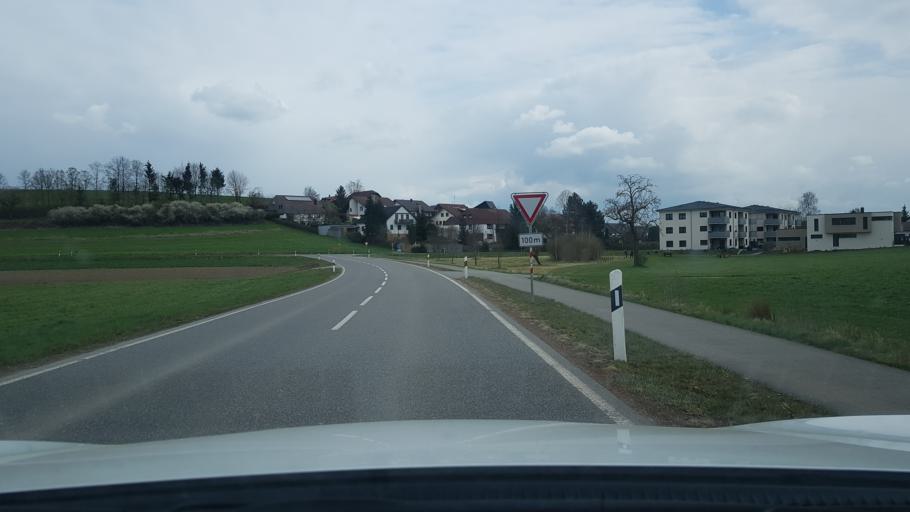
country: DE
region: Baden-Wuerttemberg
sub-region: Tuebingen Region
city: Warthausen
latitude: 48.1793
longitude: 9.7897
